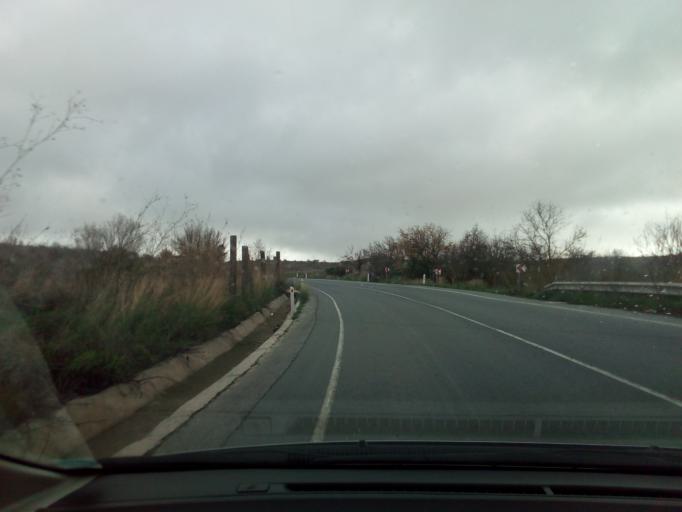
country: CY
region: Pafos
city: Tala
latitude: 34.9082
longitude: 32.4662
